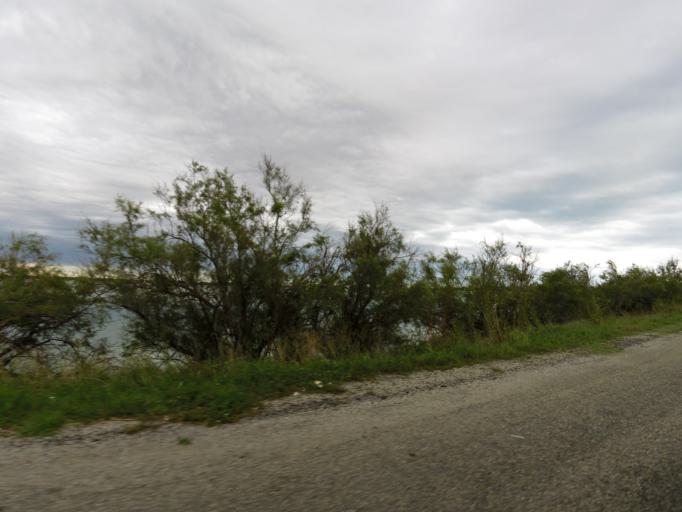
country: FR
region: Languedoc-Roussillon
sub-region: Departement du Gard
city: Le Grau-du-Roi
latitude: 43.5469
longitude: 4.1397
